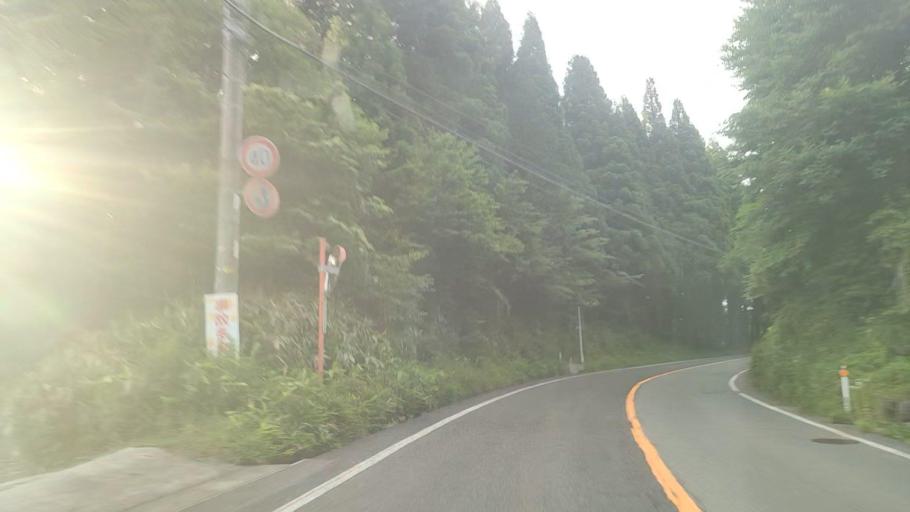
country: JP
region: Tottori
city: Kurayoshi
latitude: 35.2845
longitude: 133.6371
